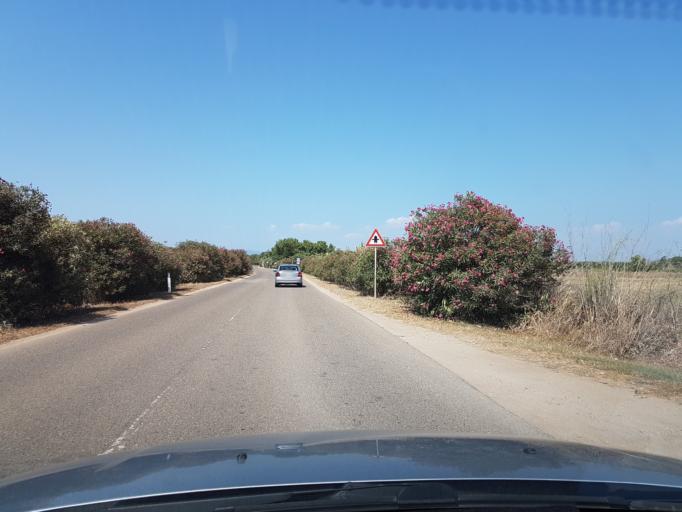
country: IT
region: Sardinia
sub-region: Provincia di Oristano
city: Cabras
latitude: 39.9223
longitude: 8.4519
